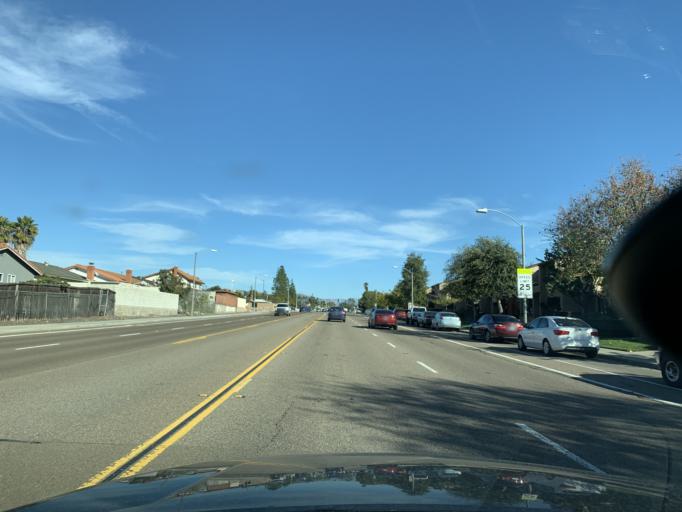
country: US
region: California
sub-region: San Diego County
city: Santee
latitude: 32.8510
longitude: -117.0018
